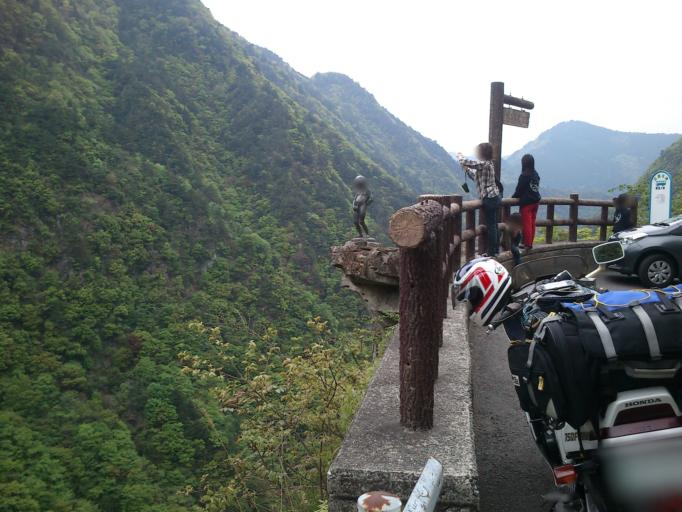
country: JP
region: Tokushima
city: Ikedacho
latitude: 33.9235
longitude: 133.8186
